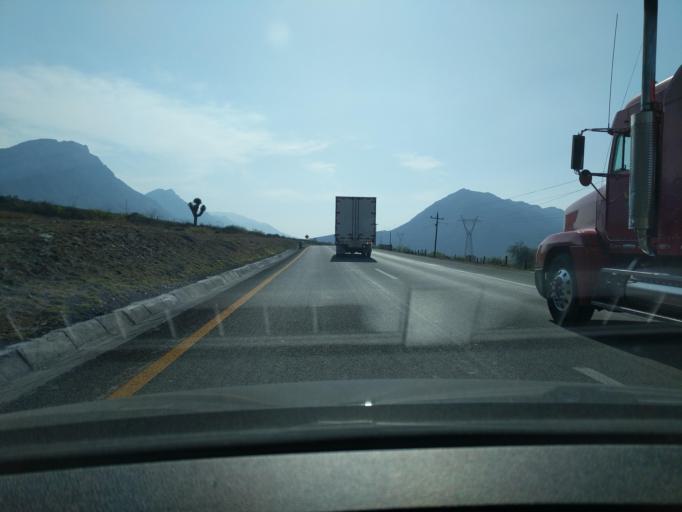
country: MX
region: Nuevo Leon
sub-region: Garcia
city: Las Torres de Guadalupe
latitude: 25.6723
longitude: -100.6928
